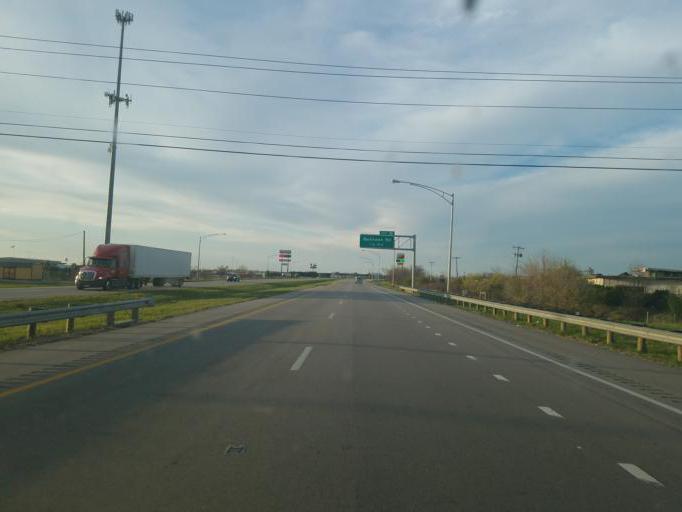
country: US
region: Ohio
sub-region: Wood County
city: Millbury
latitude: 41.5291
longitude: -83.4631
